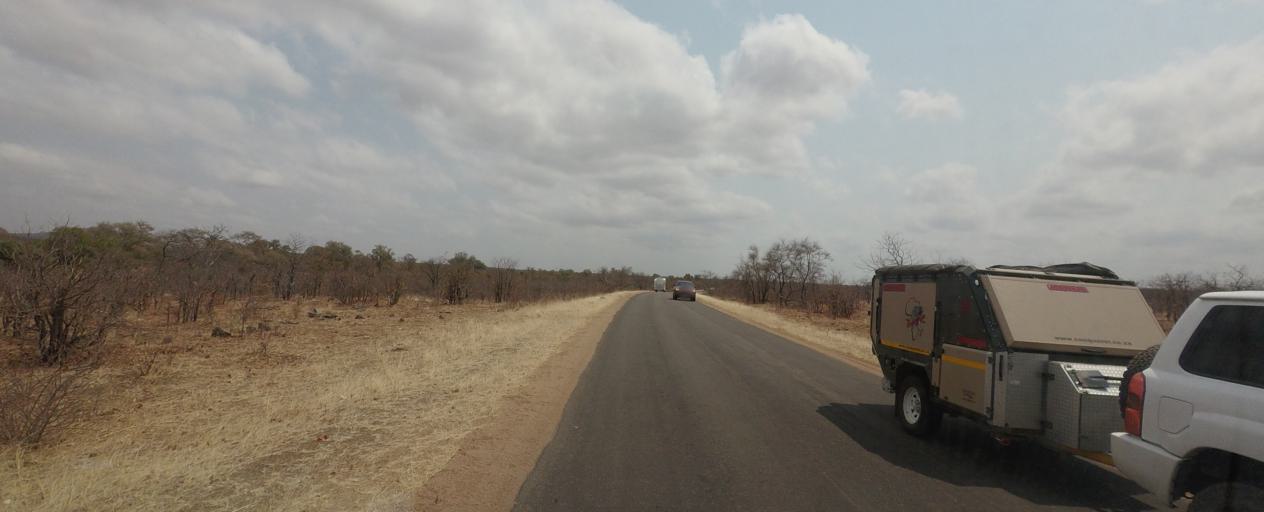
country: ZA
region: Limpopo
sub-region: Mopani District Municipality
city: Phalaborwa
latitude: -23.6100
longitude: 31.4560
